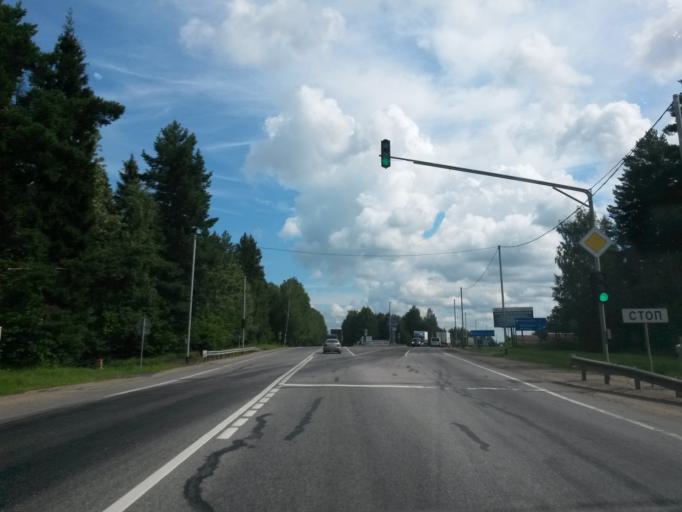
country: RU
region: Jaroslavl
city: Pereslavl'-Zalesskiy
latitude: 56.7028
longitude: 38.7877
